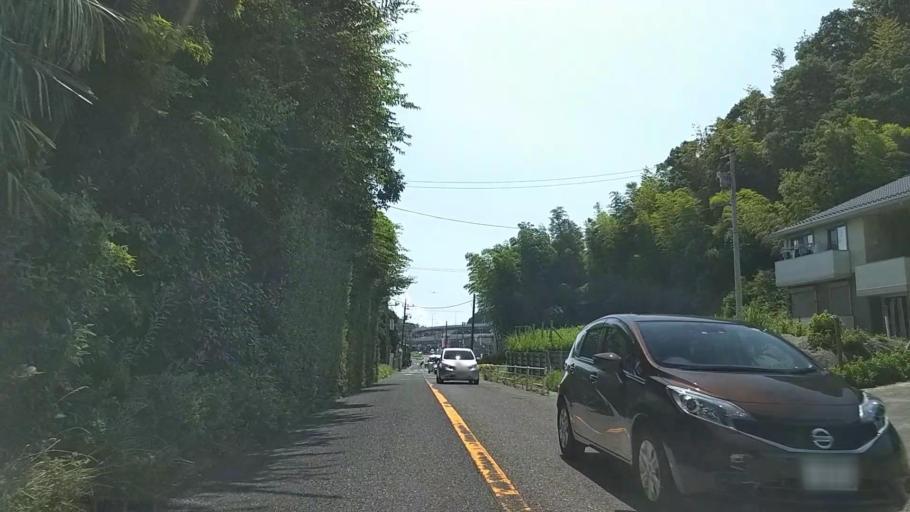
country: JP
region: Kanagawa
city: Fujisawa
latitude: 35.3621
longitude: 139.5142
